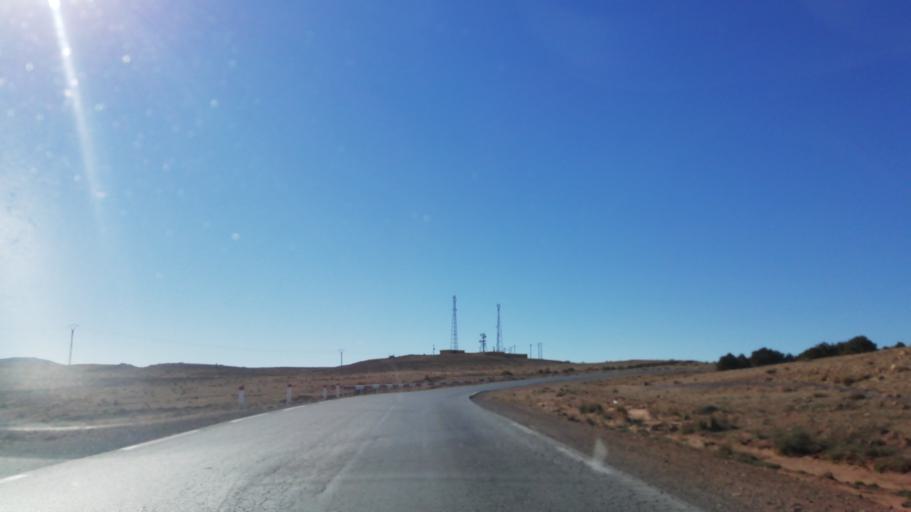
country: DZ
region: El Bayadh
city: El Bayadh
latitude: 33.6631
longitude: 1.4284
